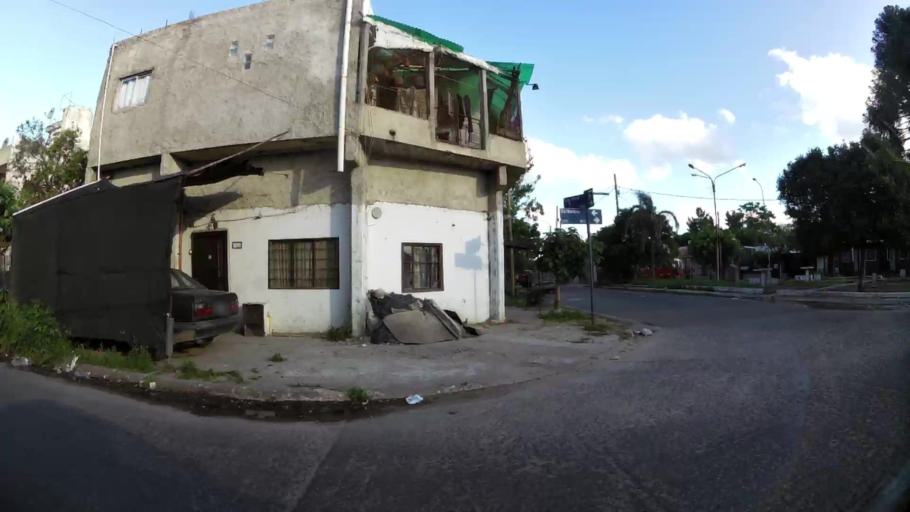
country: AR
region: Buenos Aires
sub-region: Partido de Moron
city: Moron
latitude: -34.7031
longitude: -58.6218
